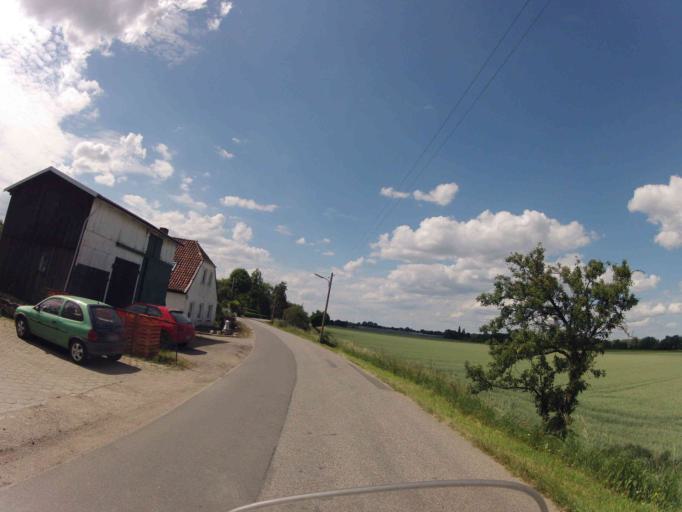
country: DE
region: Lower Saxony
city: Stelle
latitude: 53.4668
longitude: 10.1122
